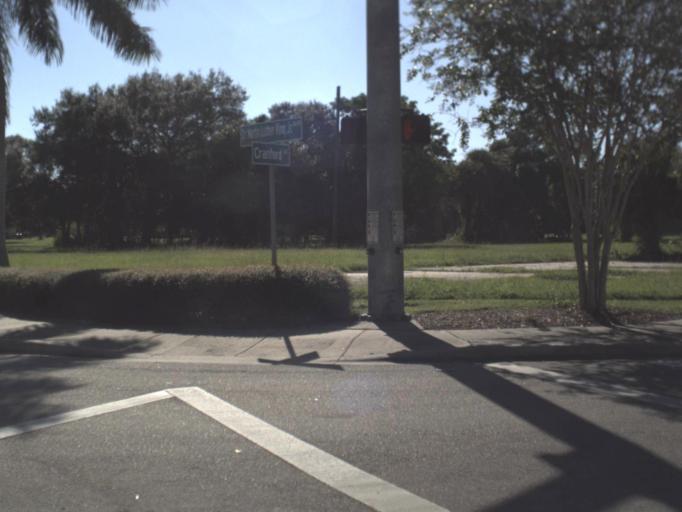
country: US
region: Florida
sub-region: Lee County
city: Fort Myers
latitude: 26.6408
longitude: -81.8583
